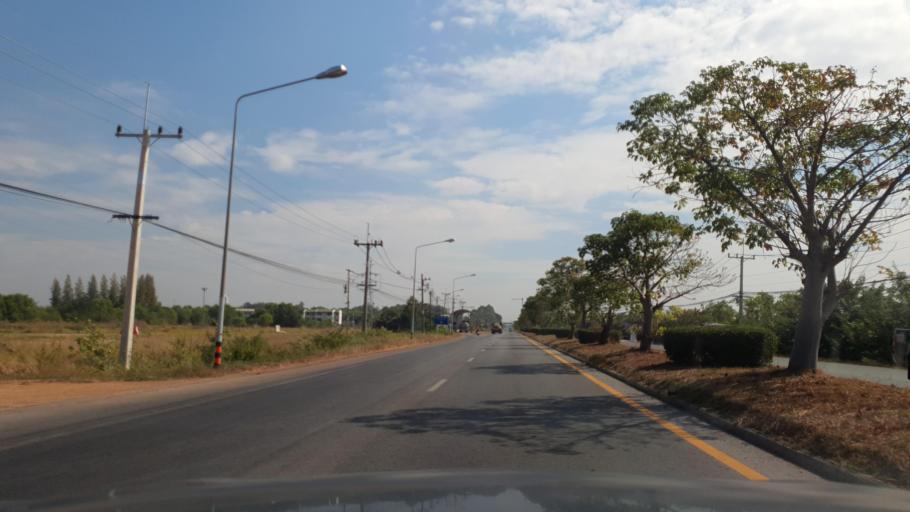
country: TH
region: Kalasin
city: Yang Talat
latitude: 16.3899
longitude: 103.3388
